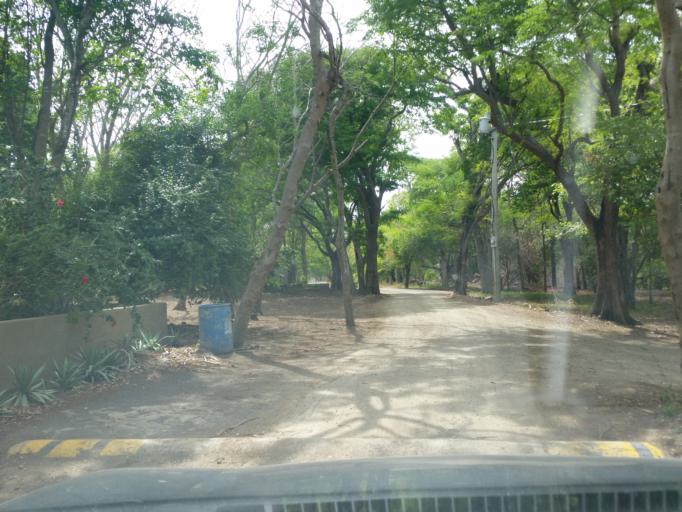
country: NI
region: Rivas
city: Tola
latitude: 11.4075
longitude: -86.0488
